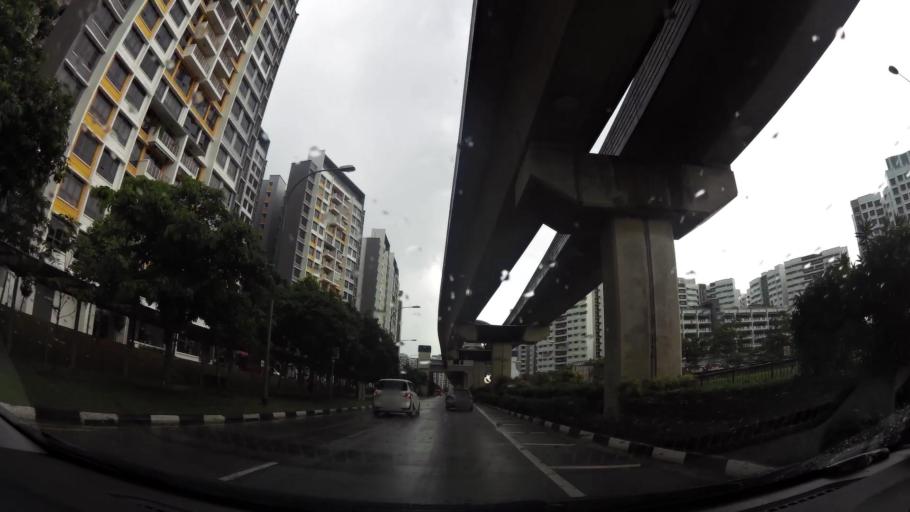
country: MY
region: Johor
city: Kampung Pasir Gudang Baru
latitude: 1.3974
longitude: 103.8882
